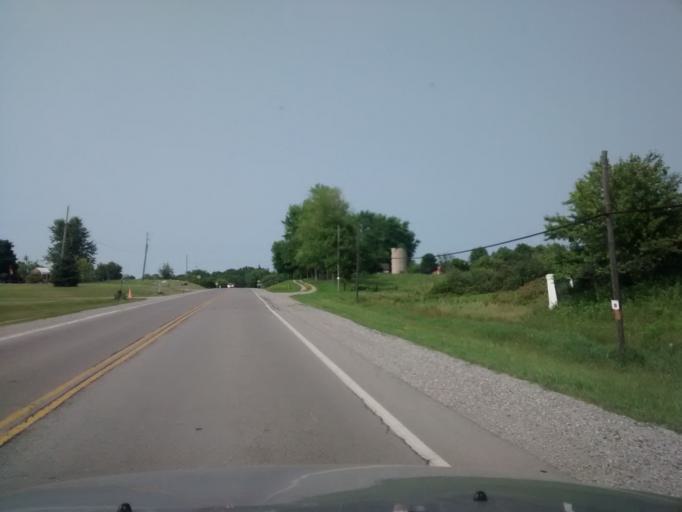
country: CA
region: Ontario
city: Ancaster
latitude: 42.9822
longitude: -79.8712
